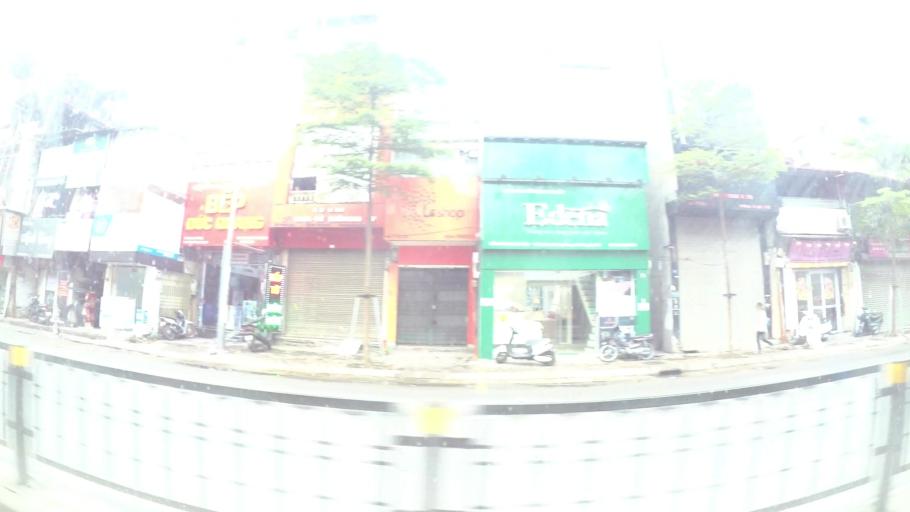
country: VN
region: Ha Noi
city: Dong Da
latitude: 21.0121
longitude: 105.8262
